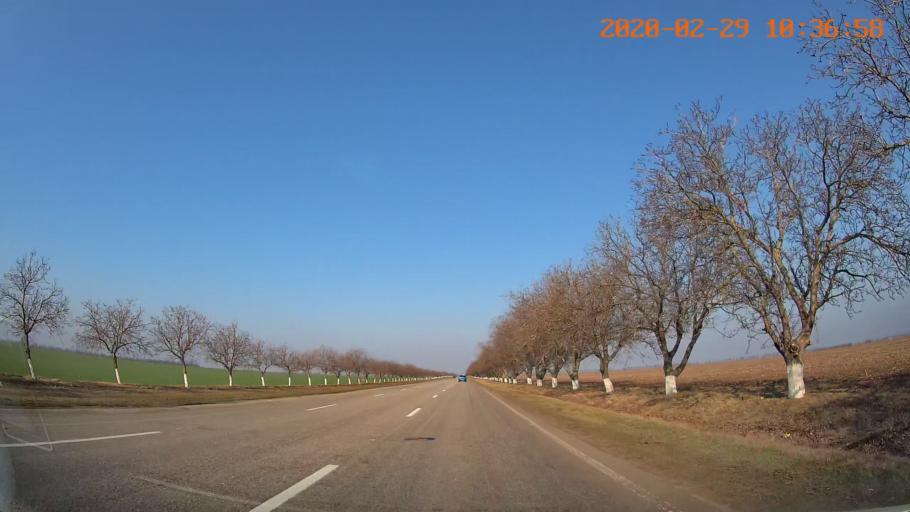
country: MD
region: Anenii Noi
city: Varnita
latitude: 47.0010
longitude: 29.4971
